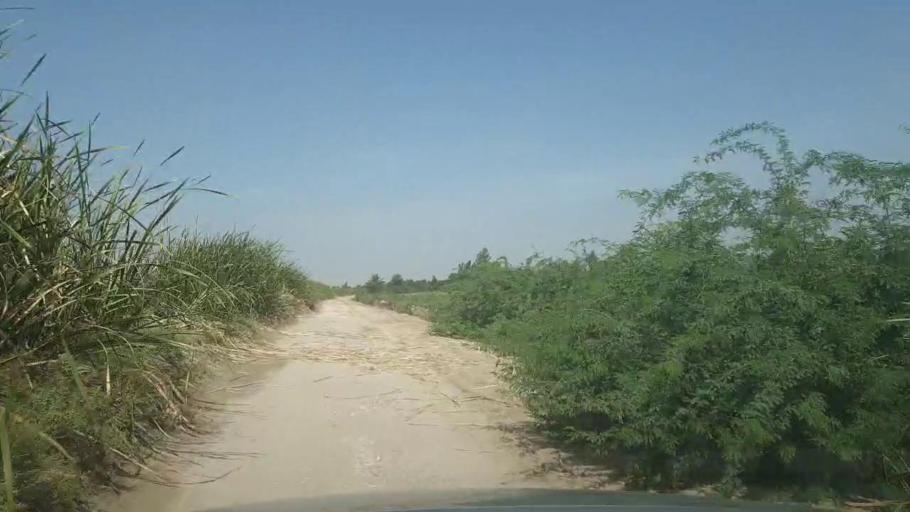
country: PK
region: Sindh
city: Khairpur
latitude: 27.3996
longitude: 69.0466
